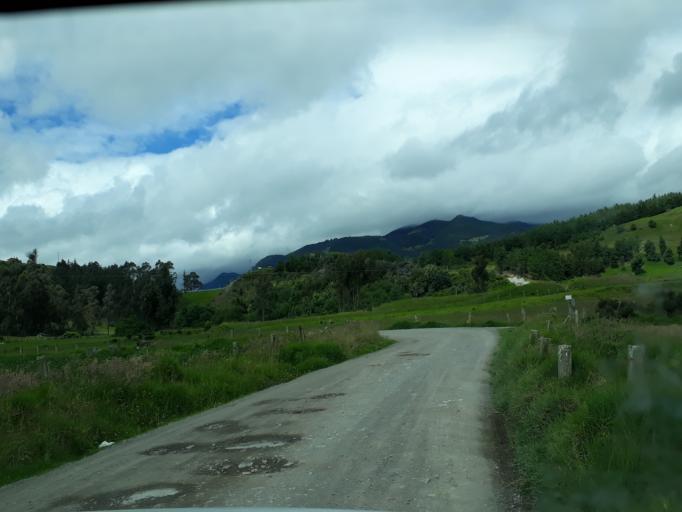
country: CO
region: Cundinamarca
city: Carmen de Carupa
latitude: 5.3067
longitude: -73.9018
